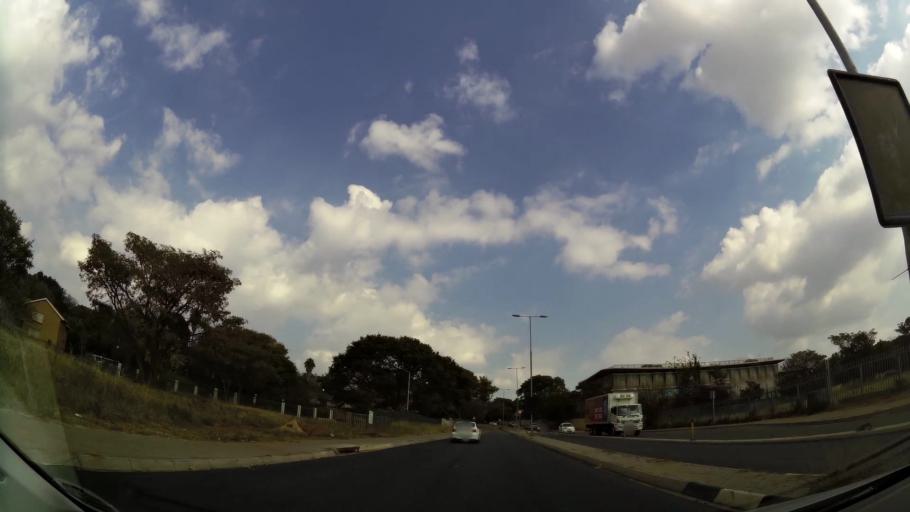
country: ZA
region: Gauteng
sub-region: City of Tshwane Metropolitan Municipality
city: Pretoria
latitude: -25.7470
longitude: 28.2905
